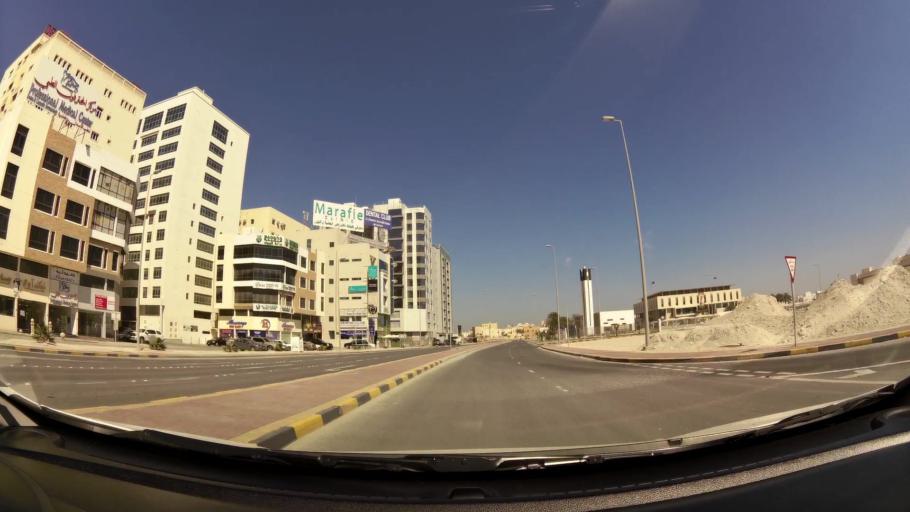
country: BH
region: Muharraq
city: Al Muharraq
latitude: 26.2642
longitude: 50.5981
